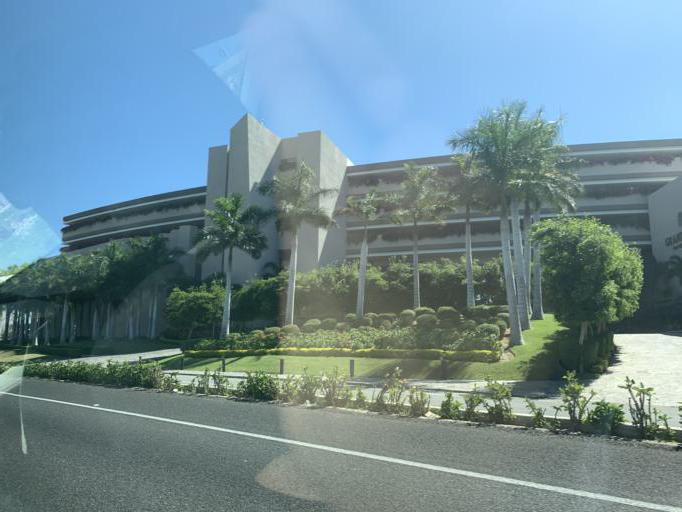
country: MX
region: Baja California Sur
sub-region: Los Cabos
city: San Jose del Cabo
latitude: 22.9684
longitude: -109.7927
